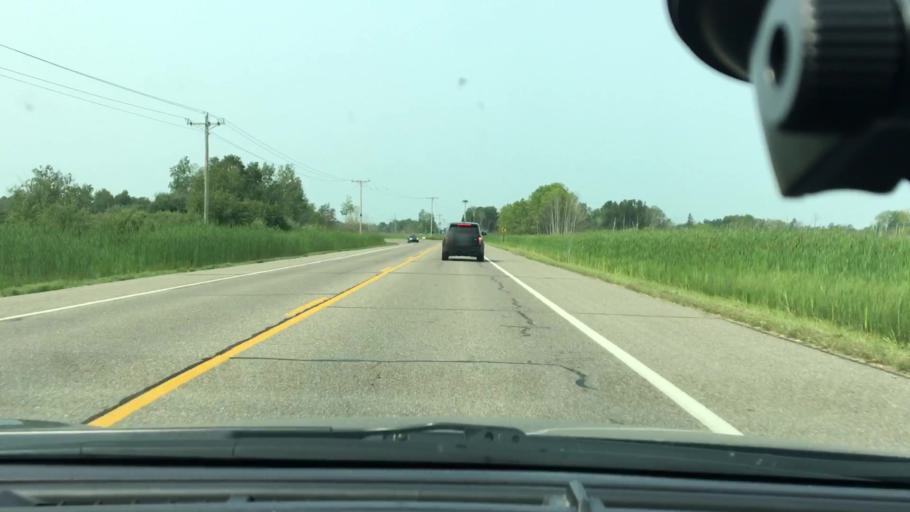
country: US
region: Minnesota
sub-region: Crow Wing County
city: Brainerd
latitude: 46.3986
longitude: -94.2186
